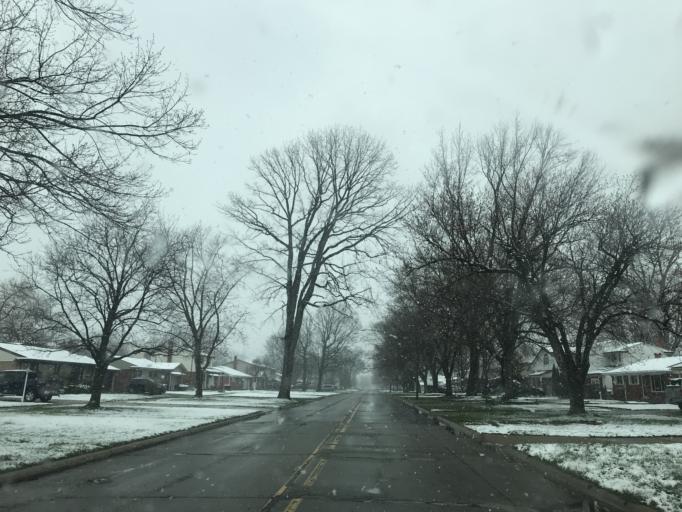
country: US
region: Michigan
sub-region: Wayne County
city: Taylor
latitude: 42.2344
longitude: -83.2495
